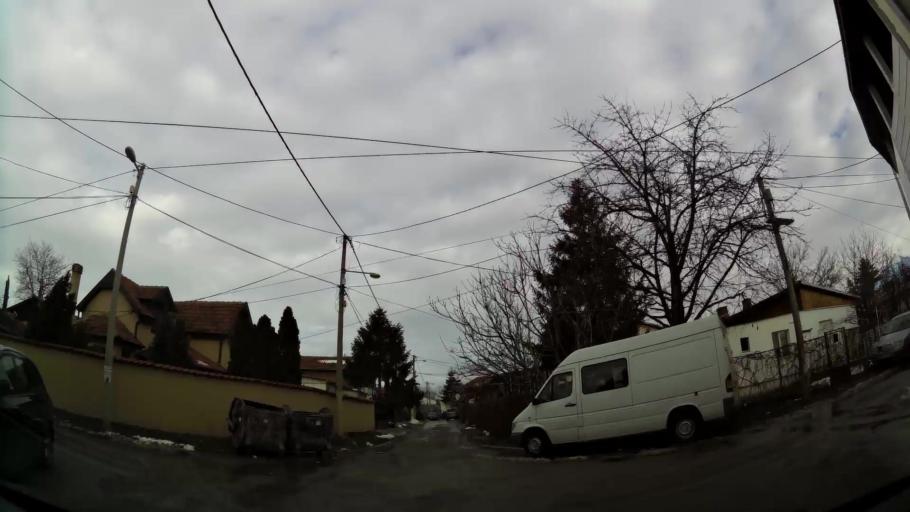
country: RS
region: Central Serbia
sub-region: Belgrade
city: Surcin
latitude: 44.8014
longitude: 20.3465
